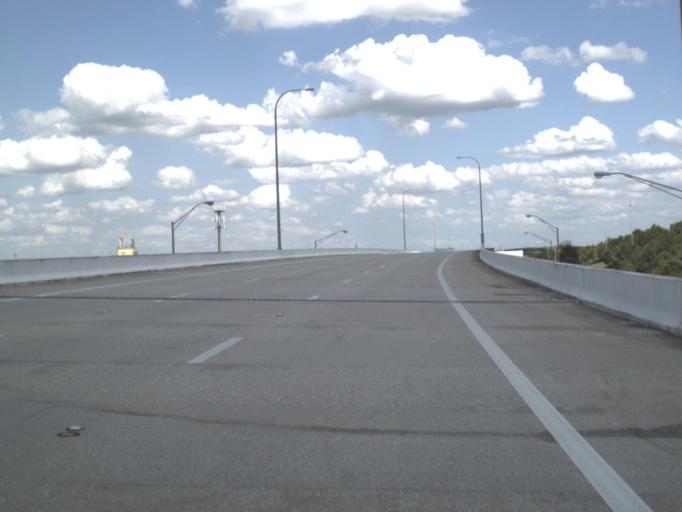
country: US
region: Florida
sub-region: Hillsborough County
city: Palm River-Clair Mel
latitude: 27.9504
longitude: -82.3864
